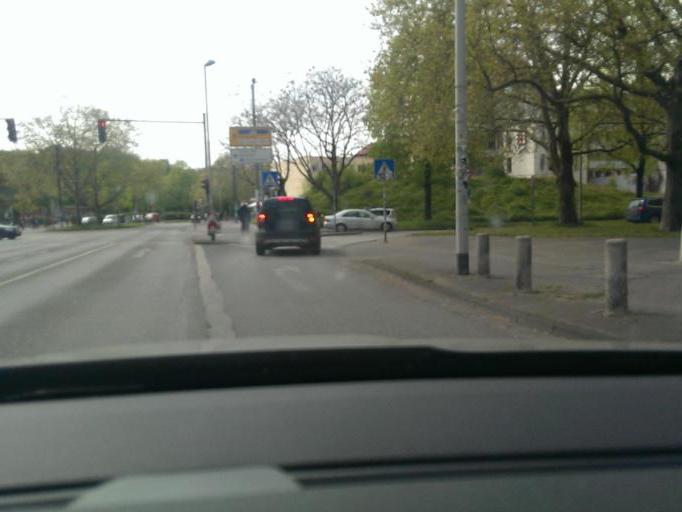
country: DE
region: Lower Saxony
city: Hannover
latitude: 52.3719
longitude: 9.7150
